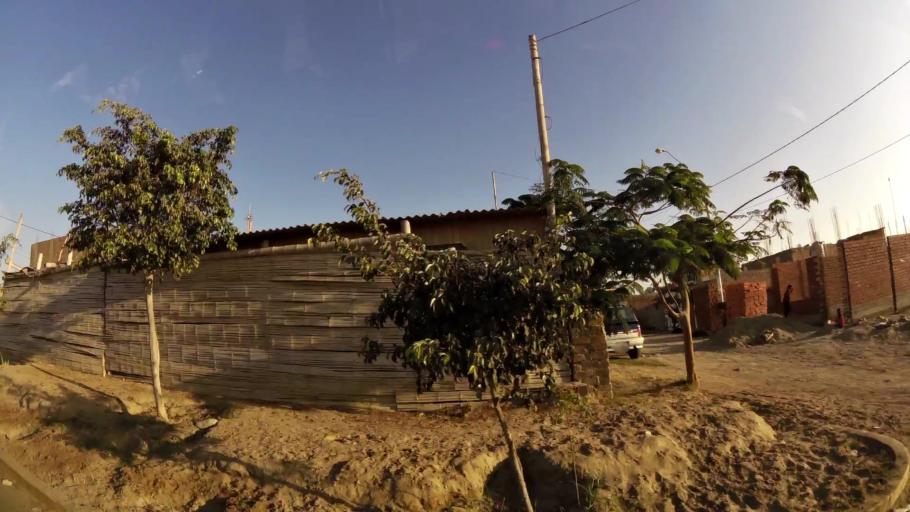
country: PE
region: Ica
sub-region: Provincia de Pisco
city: Villa Tupac Amaru
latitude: -13.7178
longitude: -76.1494
